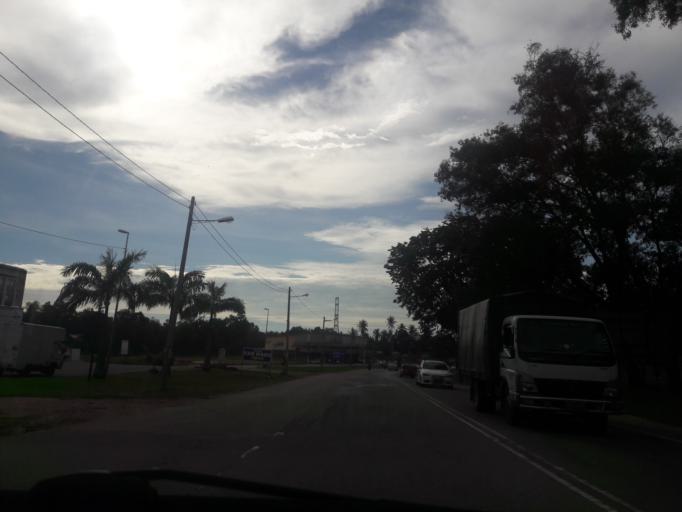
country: MY
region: Kedah
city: Sungai Petani
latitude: 5.6254
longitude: 100.5298
